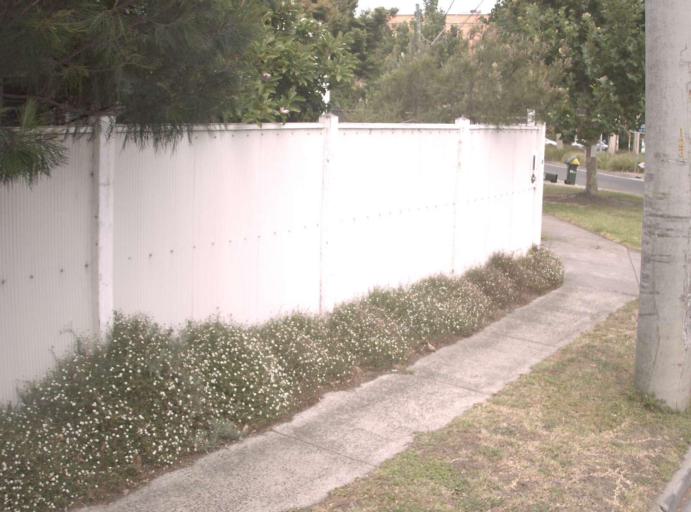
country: AU
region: Victoria
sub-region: Darebin
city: Fairfield
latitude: -37.7808
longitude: 145.0248
